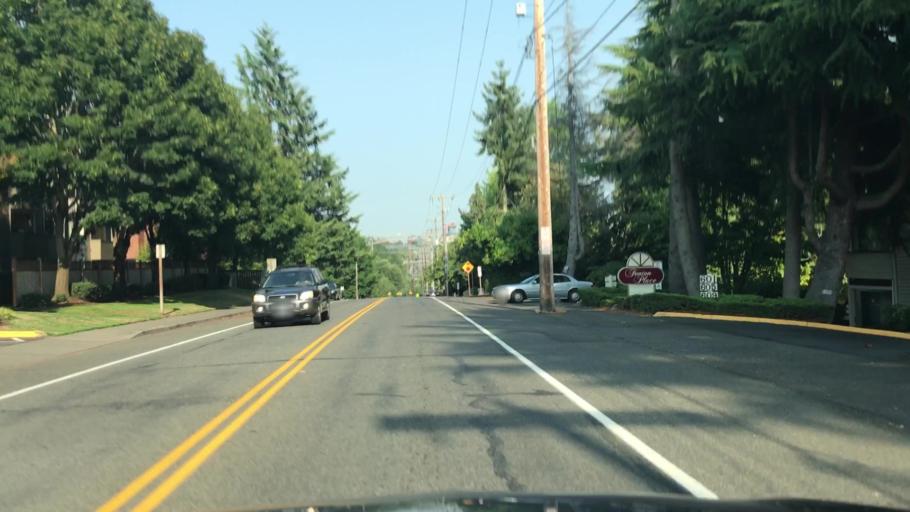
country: US
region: Washington
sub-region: King County
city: Burien
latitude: 47.4669
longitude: -122.3261
